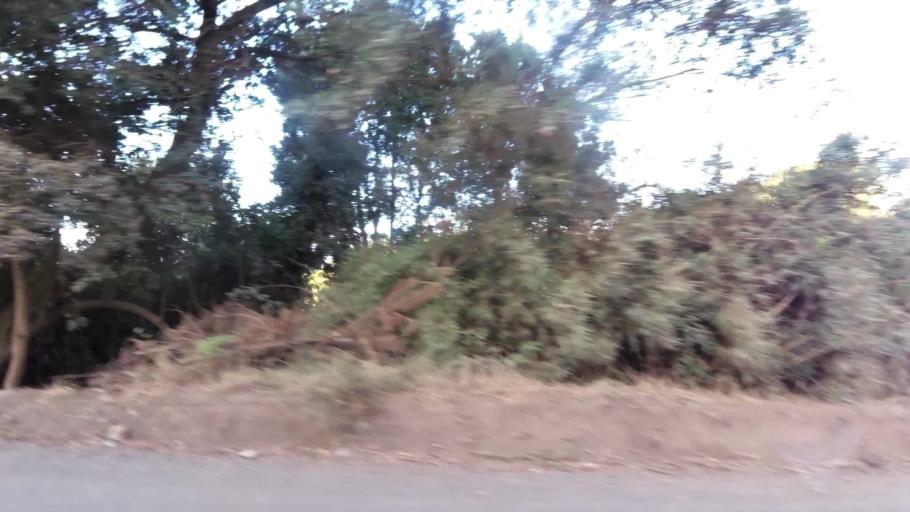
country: CL
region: Biobio
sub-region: Provincia de Concepcion
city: Concepcion
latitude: -36.8548
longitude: -73.0895
